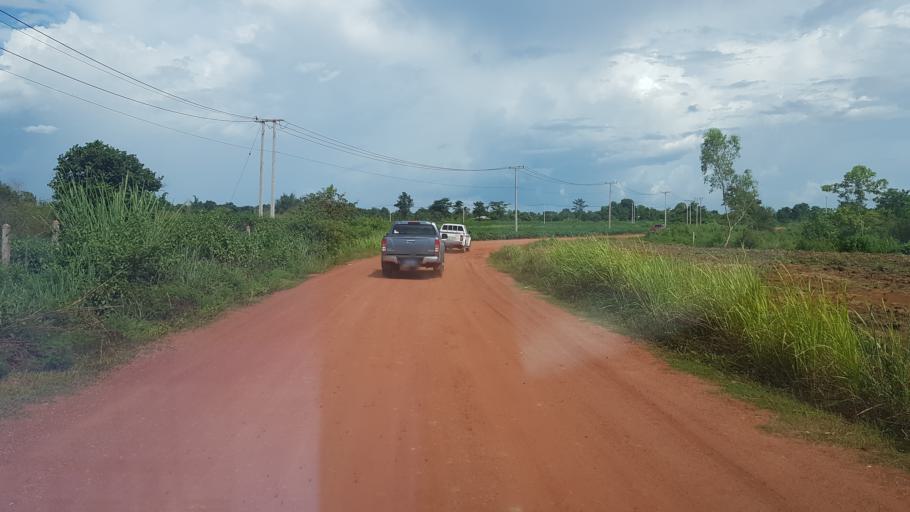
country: LA
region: Vientiane
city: Vientiane
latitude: 18.2078
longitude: 102.5673
